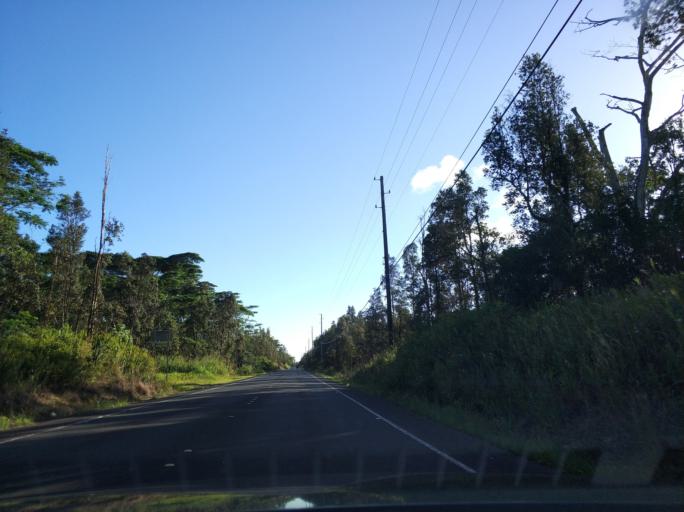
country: US
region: Hawaii
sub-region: Hawaii County
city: Leilani Estates
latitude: 19.4256
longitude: -154.9486
